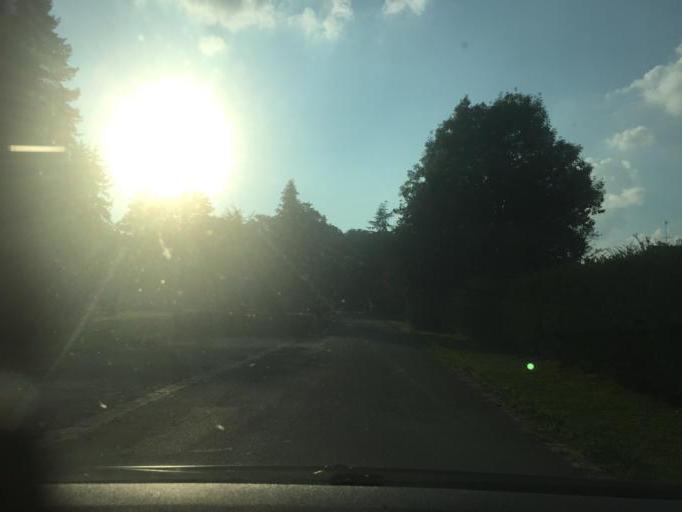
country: FR
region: Ile-de-France
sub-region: Departement des Yvelines
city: Jouy-en-Josas
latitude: 48.7631
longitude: 2.1625
